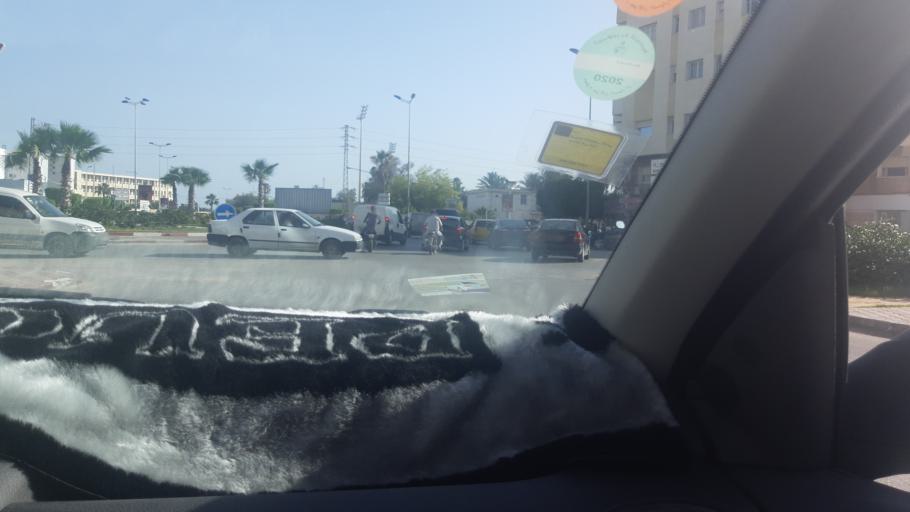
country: TN
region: Safaqis
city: Sfax
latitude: 34.7364
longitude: 10.7489
